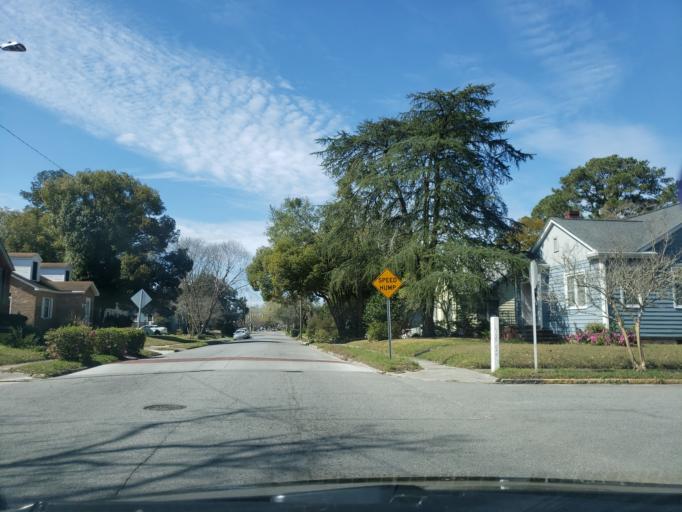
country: US
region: Georgia
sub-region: Chatham County
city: Thunderbolt
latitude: 32.0409
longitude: -81.0859
